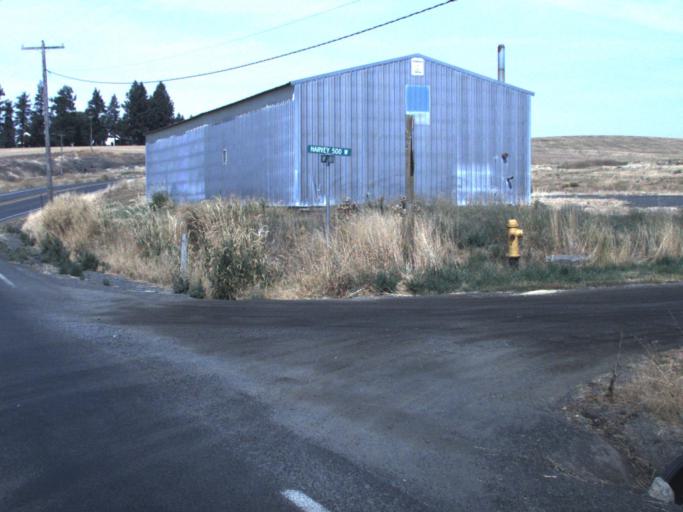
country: US
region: Idaho
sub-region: Benewah County
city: Plummer
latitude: 47.2840
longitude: -117.1614
